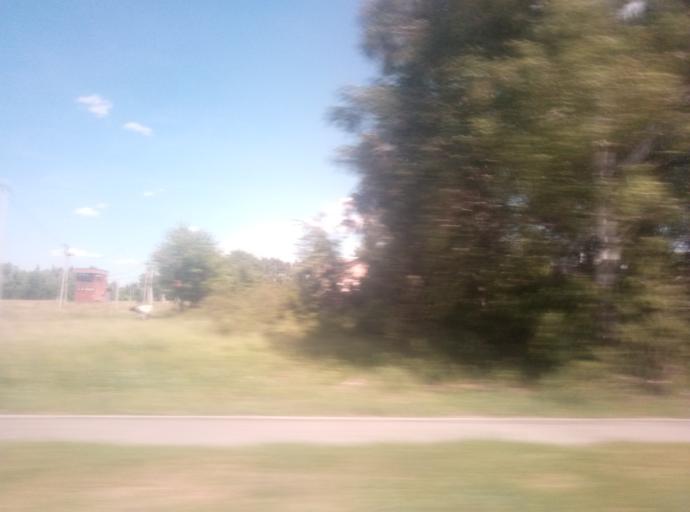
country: RU
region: Tula
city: Kireyevsk
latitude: 54.0176
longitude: 37.9116
